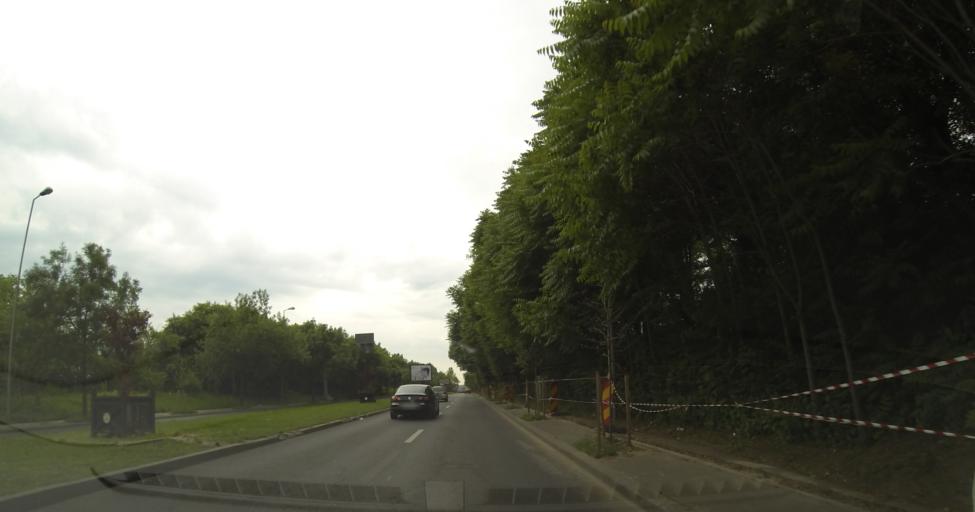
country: RO
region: Bucuresti
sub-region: Municipiul Bucuresti
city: Bucuresti
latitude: 44.4389
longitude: 26.0600
